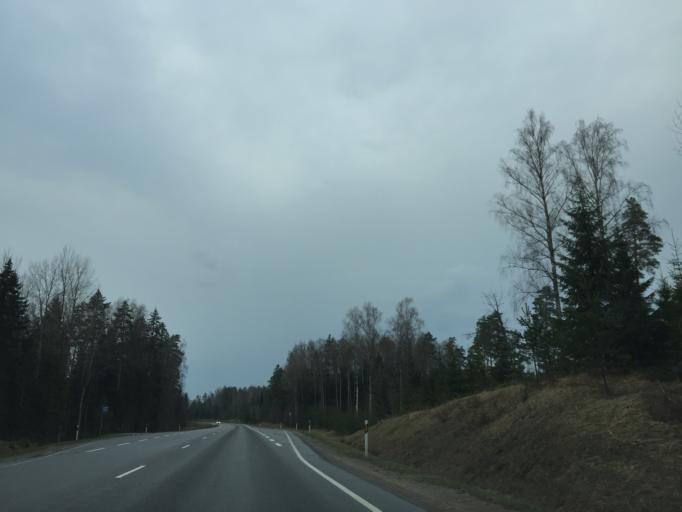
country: EE
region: Tartu
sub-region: UElenurme vald
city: Ulenurme
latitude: 58.1219
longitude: 26.7318
